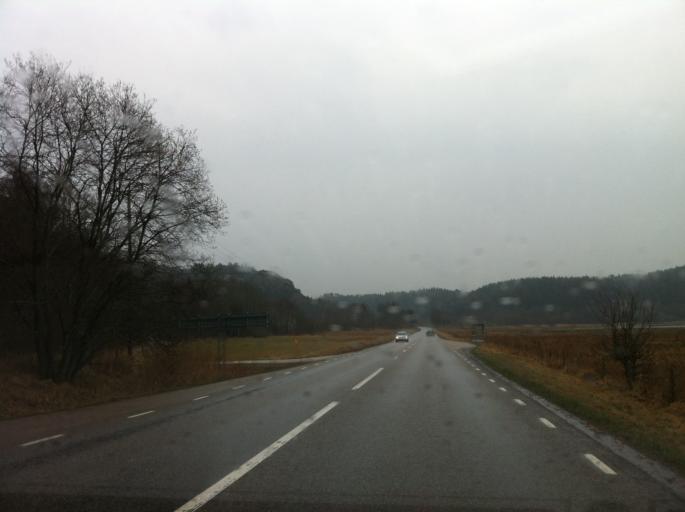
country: SE
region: Vaestra Goetaland
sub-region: Lysekils Kommun
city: Brastad
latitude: 58.4618
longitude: 11.4556
